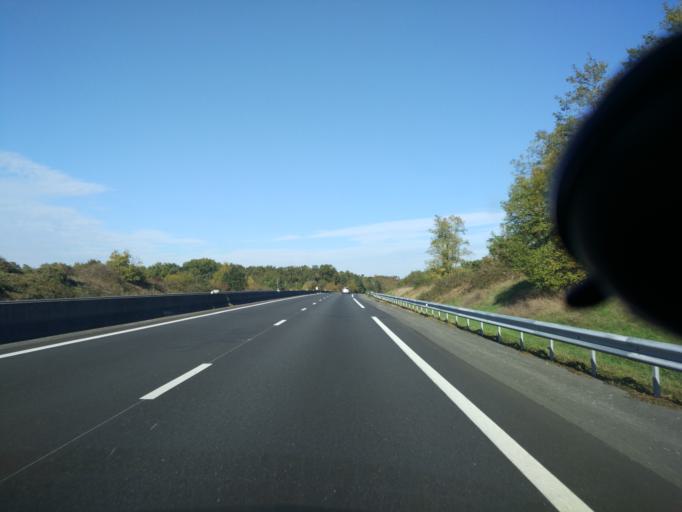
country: FR
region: Poitou-Charentes
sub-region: Departement de la Charente
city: La Couronne
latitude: 45.6029
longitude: 0.0734
